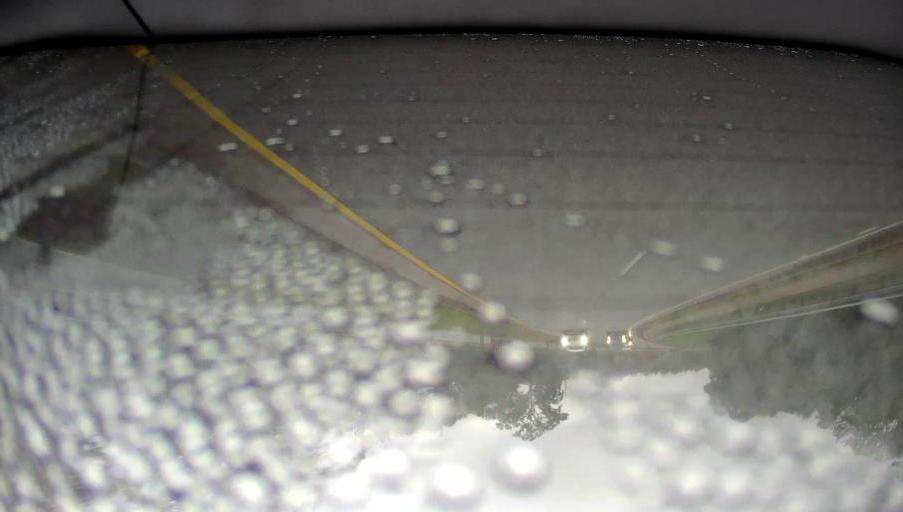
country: US
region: Georgia
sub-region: Houston County
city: Centerville
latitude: 32.5853
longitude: -83.6617
